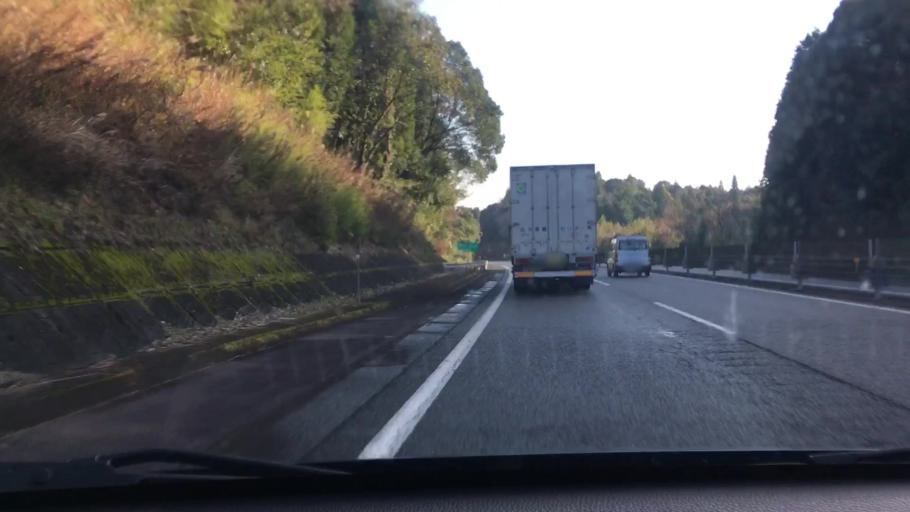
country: JP
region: Kagoshima
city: Okuchi-shinohara
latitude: 31.9147
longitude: 130.7035
